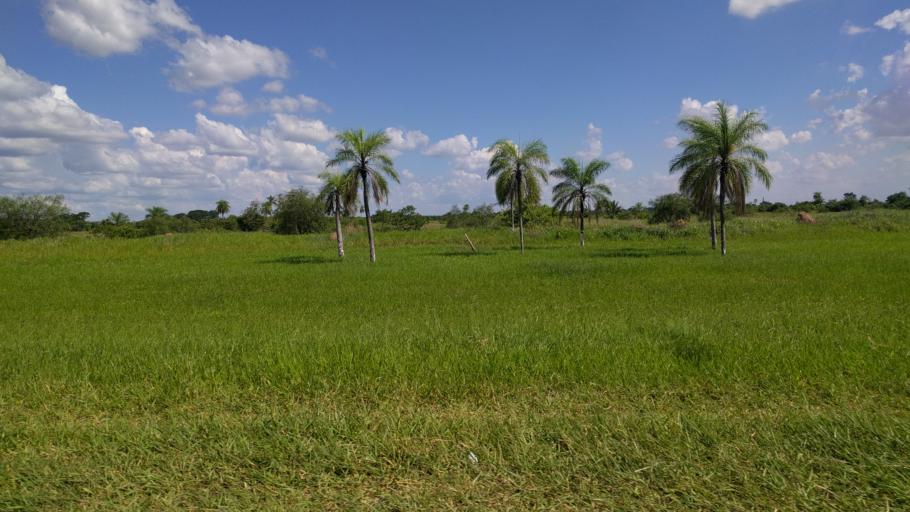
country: BO
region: Santa Cruz
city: La Belgica
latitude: -17.6554
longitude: -63.1535
